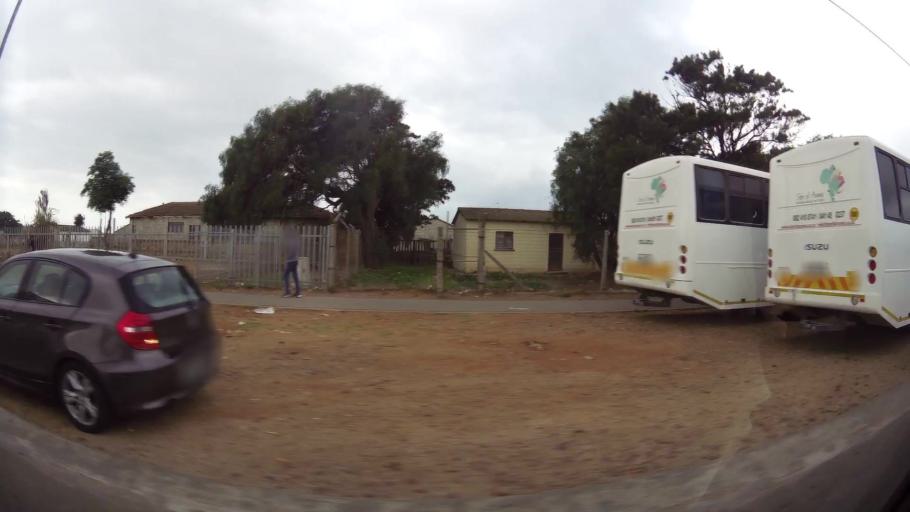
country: ZA
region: Eastern Cape
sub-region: Nelson Mandela Bay Metropolitan Municipality
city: Port Elizabeth
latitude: -33.9039
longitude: 25.5987
